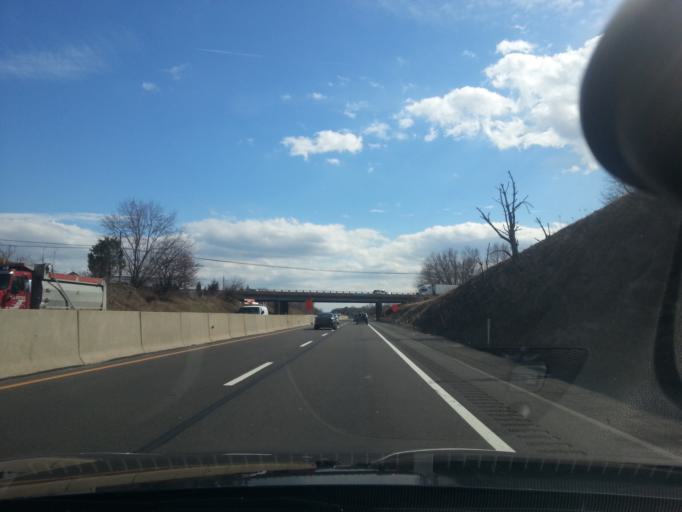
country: US
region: Pennsylvania
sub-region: Montgomery County
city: Harleysville
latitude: 40.3017
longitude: -75.3705
